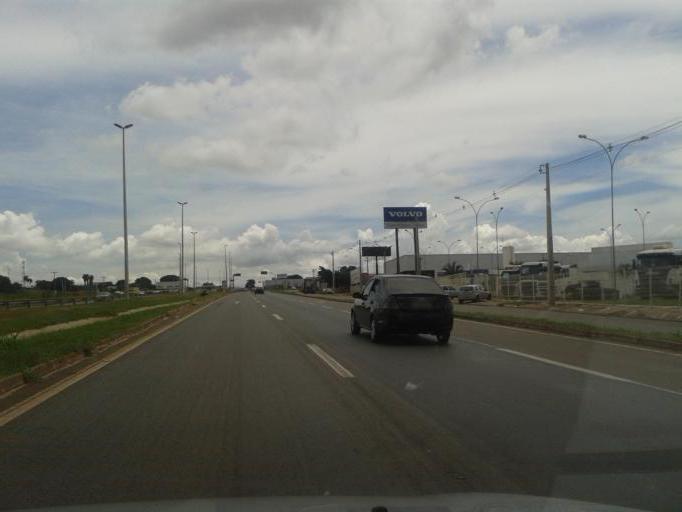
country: BR
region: Goias
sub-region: Aparecida De Goiania
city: Aparecida de Goiania
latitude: -16.8299
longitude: -49.2428
